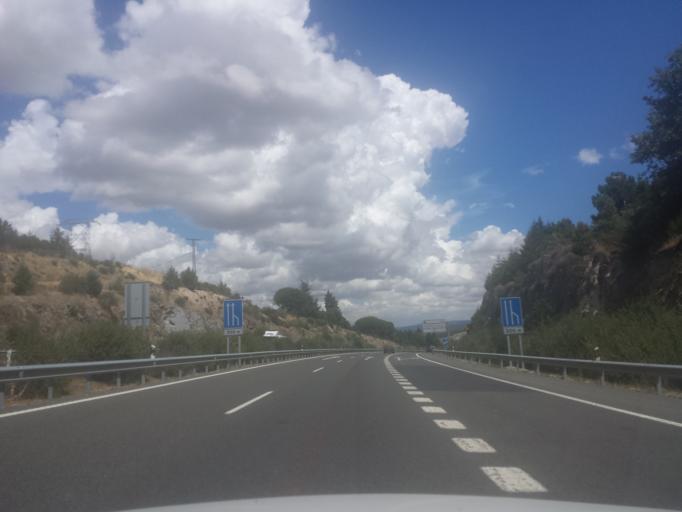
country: ES
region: Castille and Leon
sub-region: Provincia de Salamanca
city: Penacaballera
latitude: 40.3426
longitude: -5.8503
